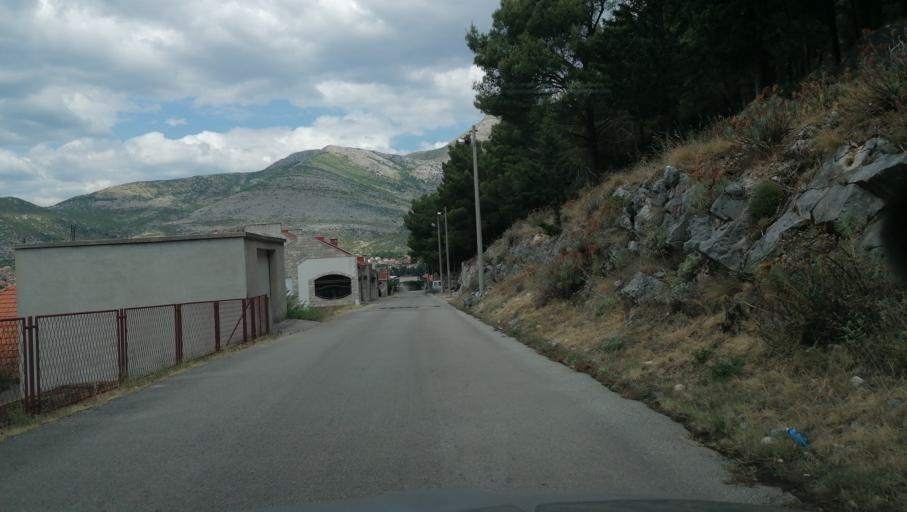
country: BA
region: Republika Srpska
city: Trebinje
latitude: 42.7091
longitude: 18.3582
